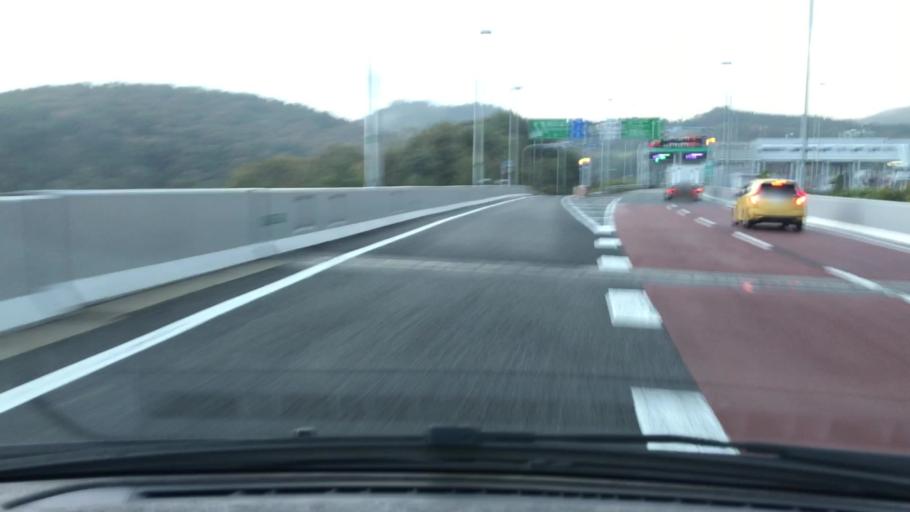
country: JP
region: Hyogo
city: Sandacho
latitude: 34.8306
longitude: 135.2571
